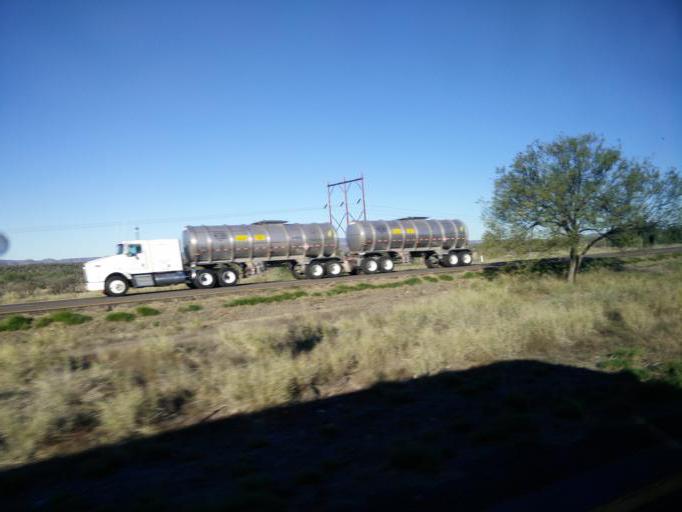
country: MX
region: Sonora
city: Heroica Guaymas
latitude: 28.1531
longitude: -110.9777
